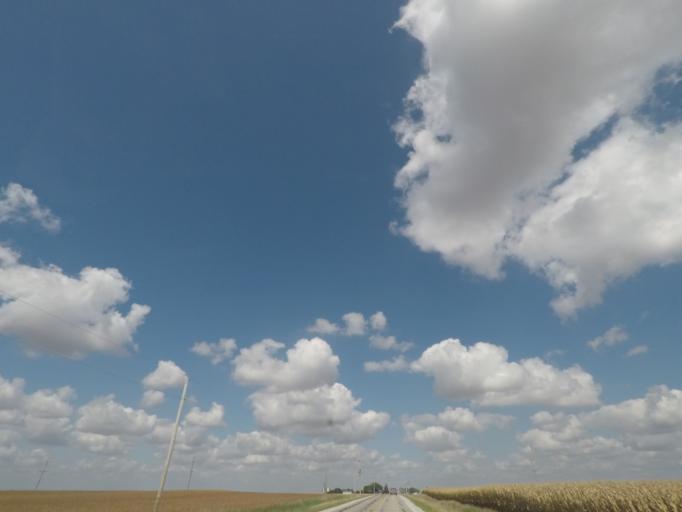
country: US
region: Iowa
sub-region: Story County
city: Nevada
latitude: 42.0328
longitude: -93.4058
